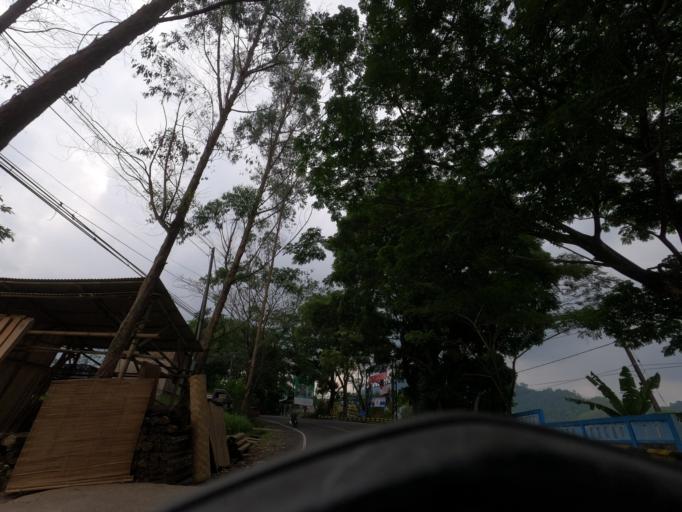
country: ID
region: West Java
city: Sukabumi
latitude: -6.7730
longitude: 107.0634
